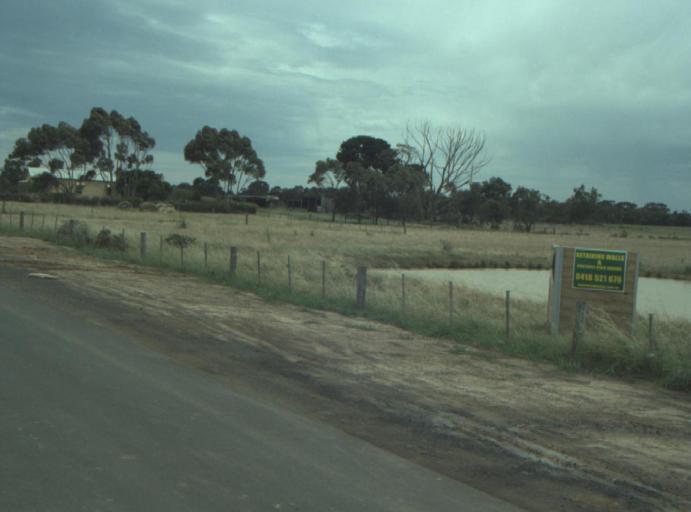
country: AU
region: Victoria
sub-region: Greater Geelong
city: Leopold
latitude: -38.1994
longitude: 144.4530
